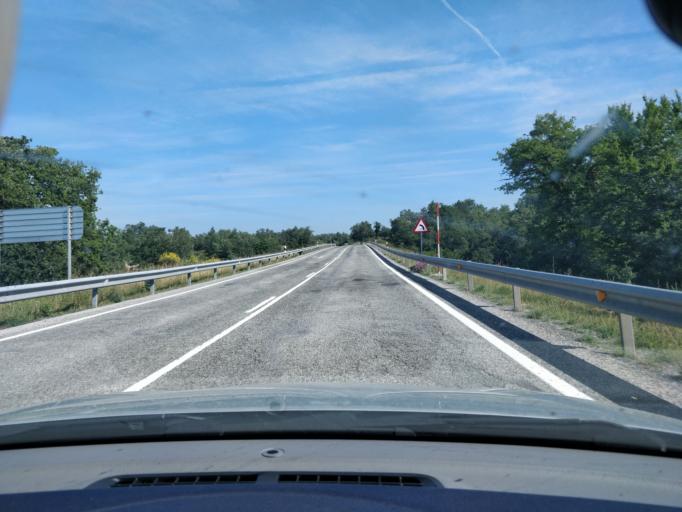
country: ES
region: Cantabria
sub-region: Provincia de Cantabria
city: San Pedro del Romeral
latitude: 42.9617
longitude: -3.7764
